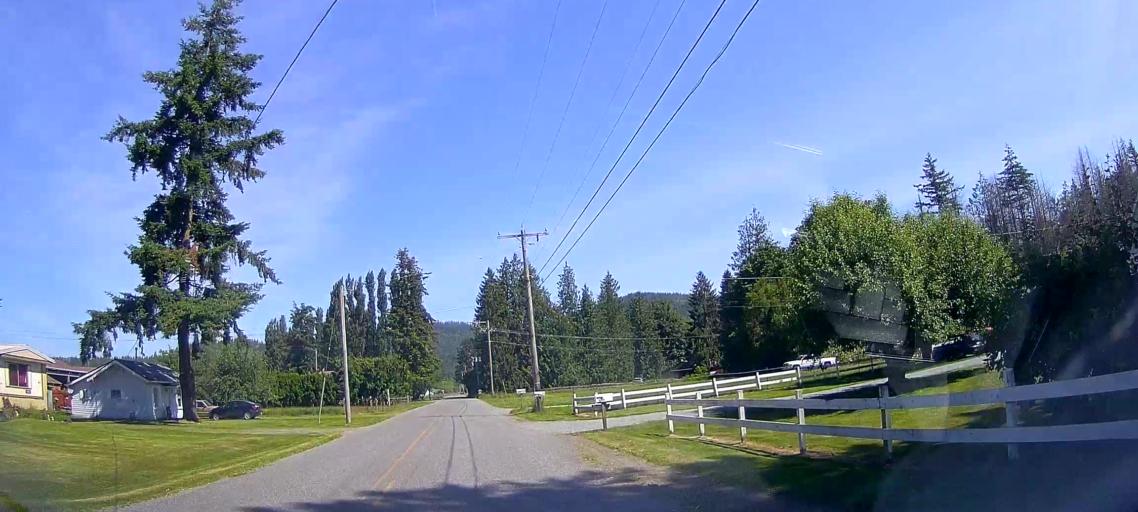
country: US
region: Washington
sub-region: Skagit County
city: Sedro-Woolley
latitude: 48.5222
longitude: -122.2906
